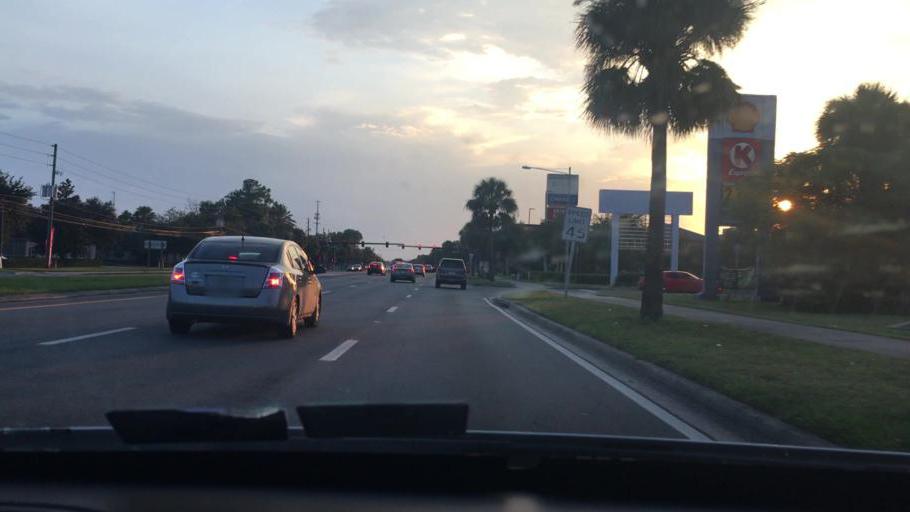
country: US
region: Florida
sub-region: Seminole County
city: Goldenrod
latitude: 28.5976
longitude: -81.2883
